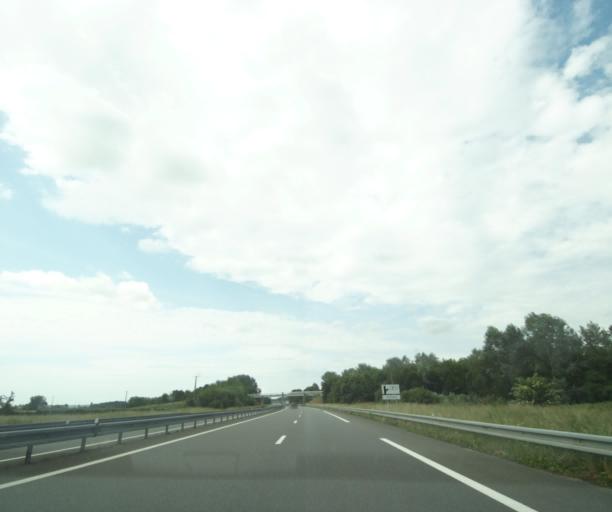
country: FR
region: Pays de la Loire
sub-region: Departement de Maine-et-Loire
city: Brion
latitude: 47.4528
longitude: -0.1779
